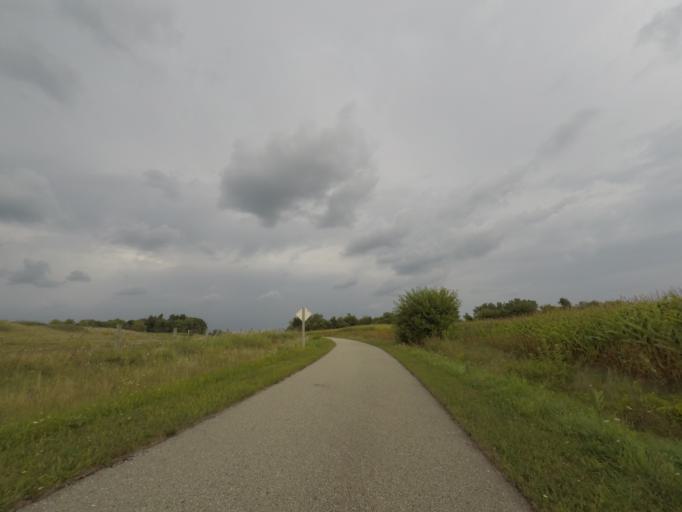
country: US
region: Wisconsin
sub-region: Jefferson County
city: Jefferson
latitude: 42.9777
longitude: -88.8221
